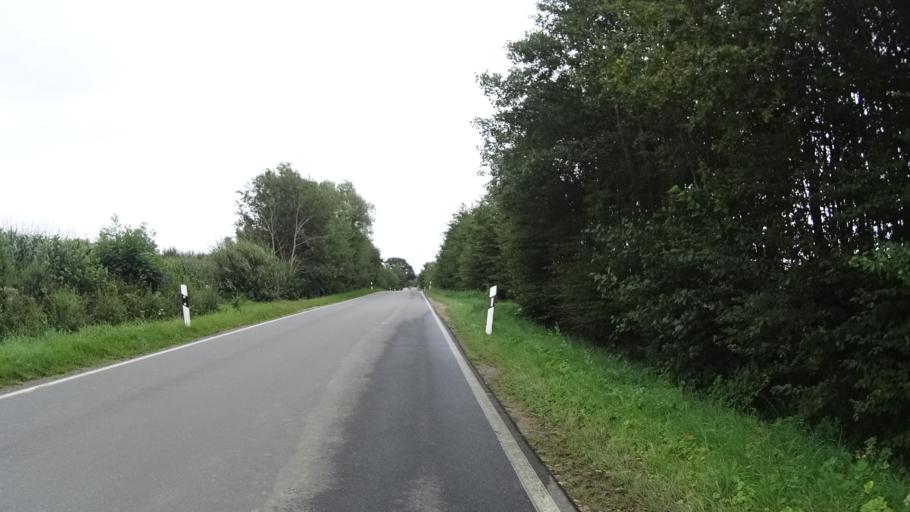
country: DE
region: Schleswig-Holstein
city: Labenz
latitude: 53.7140
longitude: 10.5053
